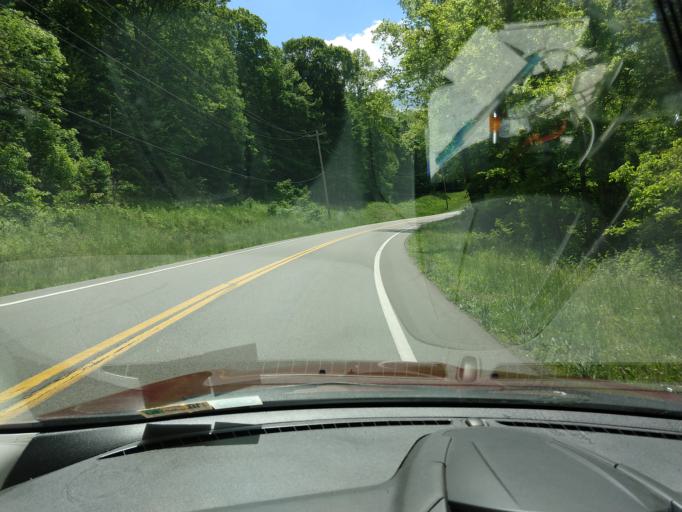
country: US
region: West Virginia
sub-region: Gilmer County
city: Glenville
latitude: 38.8880
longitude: -80.7195
